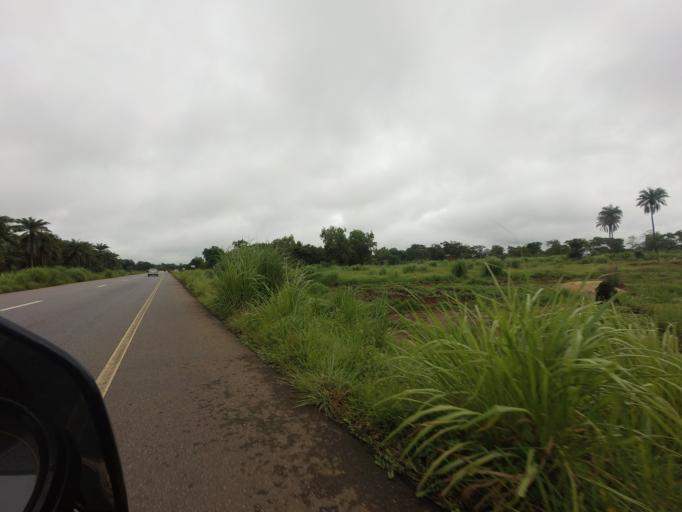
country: SL
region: Northern Province
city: Kambia
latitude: 9.0986
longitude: -12.9165
